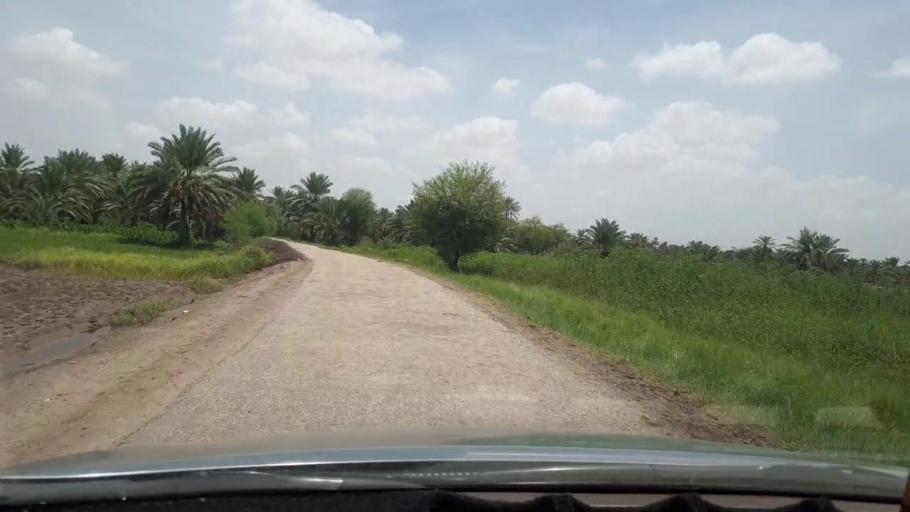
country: PK
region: Sindh
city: Khairpur
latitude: 27.4507
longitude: 68.7843
